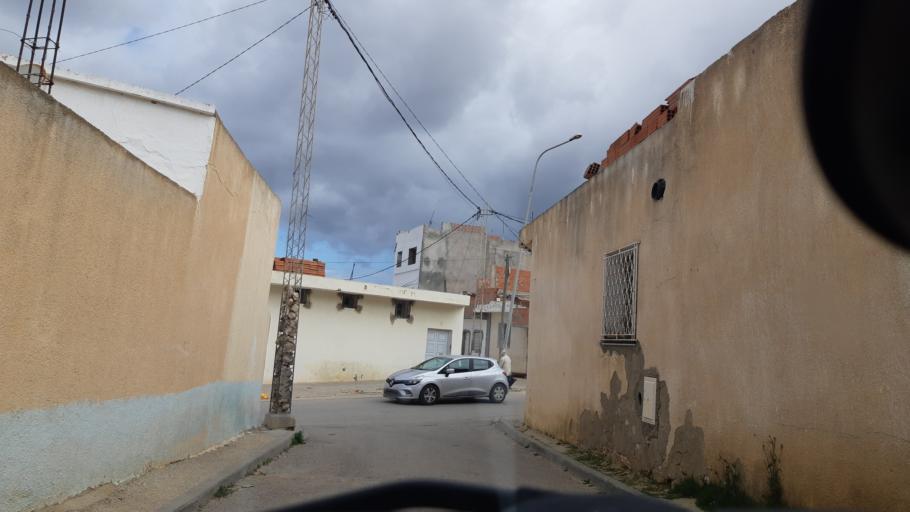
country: TN
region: Susah
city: Akouda
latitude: 35.8700
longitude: 10.5239
